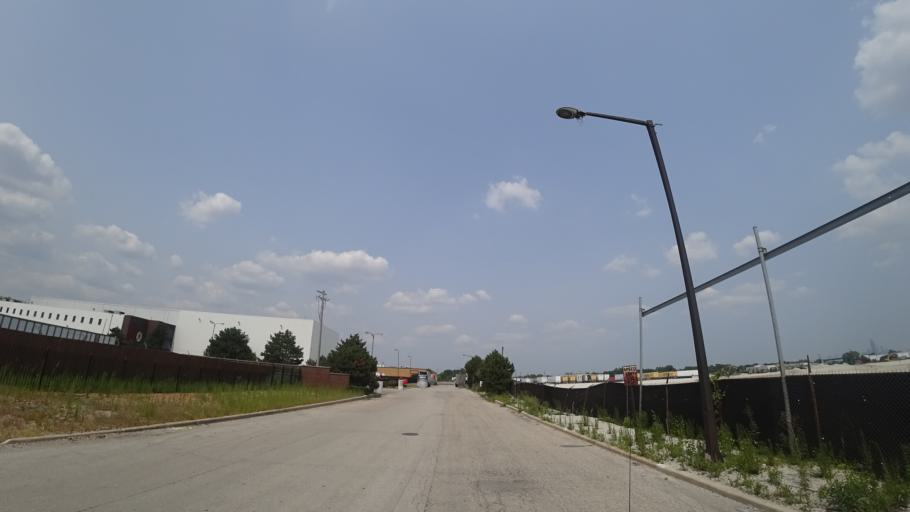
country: US
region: Illinois
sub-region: Cook County
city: Cicero
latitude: 41.8278
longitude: -87.7353
